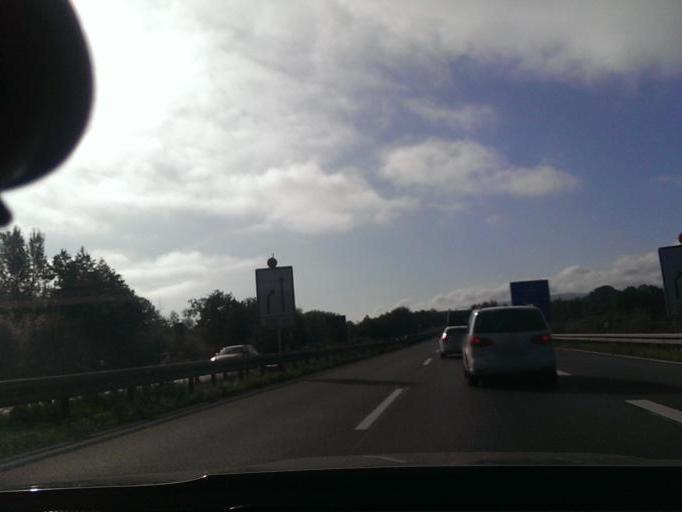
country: DE
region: Lower Saxony
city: Vienenburg
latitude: 51.9560
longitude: 10.5808
